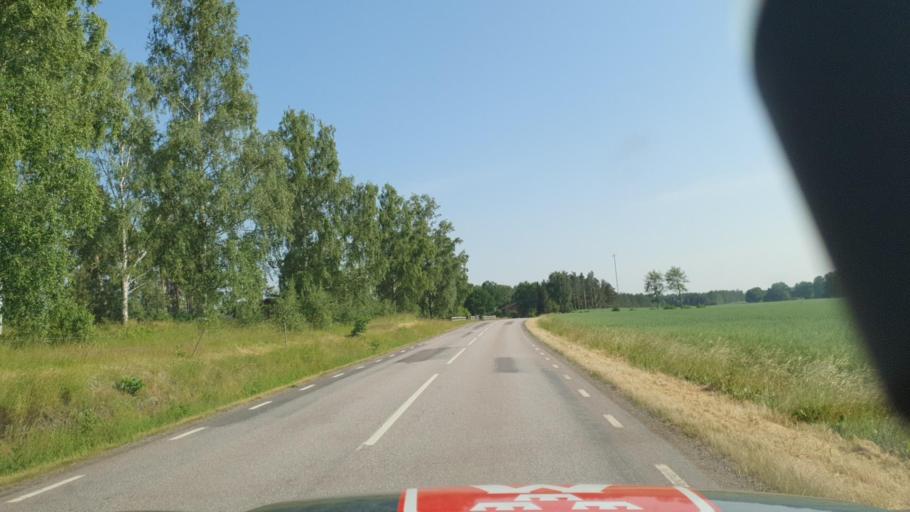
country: SE
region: Kalmar
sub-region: Kalmar Kommun
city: Ljungbyholm
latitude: 56.6657
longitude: 16.1574
